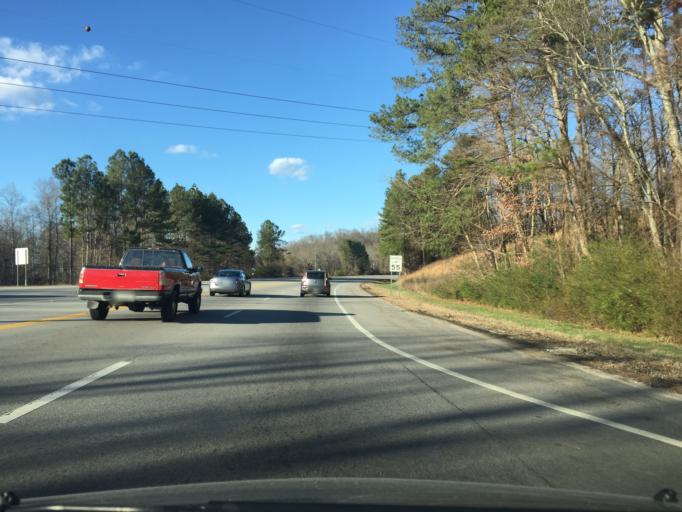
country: US
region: Tennessee
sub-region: Hamilton County
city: Harrison
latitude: 35.1261
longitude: -85.1252
